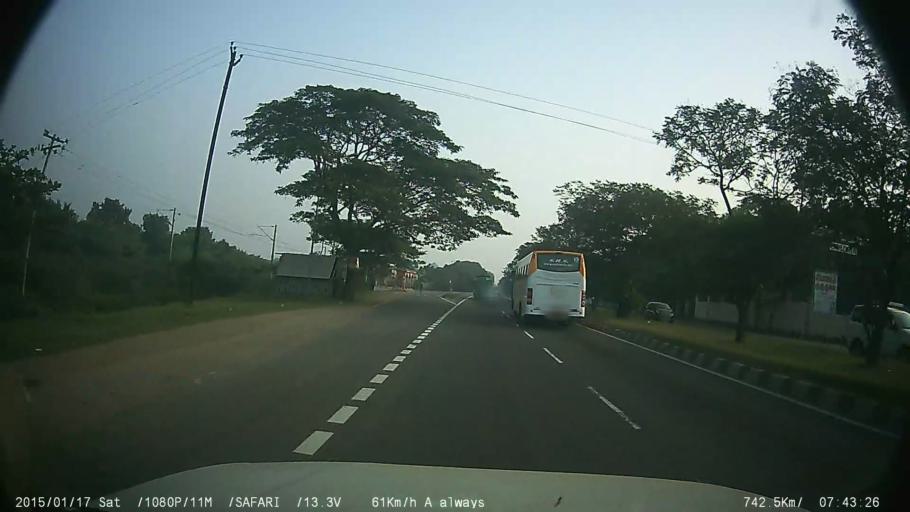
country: IN
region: Tamil Nadu
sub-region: Kancheepuram
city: Madambakkam
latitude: 12.8133
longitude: 80.0319
